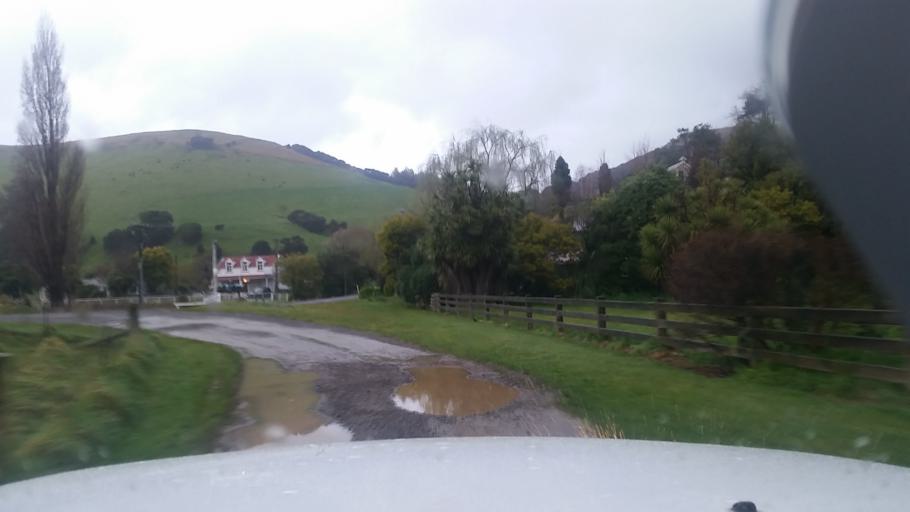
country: NZ
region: Canterbury
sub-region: Christchurch City
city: Christchurch
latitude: -43.7800
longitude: 172.9071
